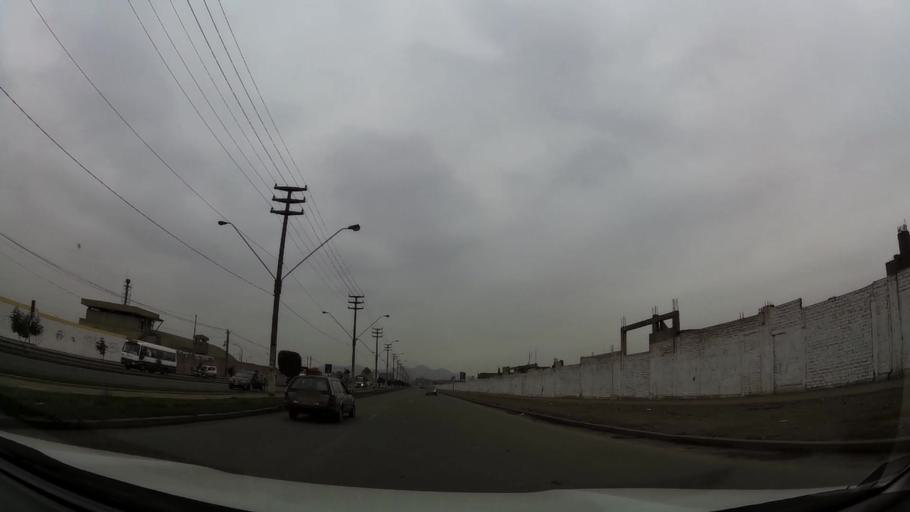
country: PE
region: Lima
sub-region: Lima
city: Vitarte
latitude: -12.0338
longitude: -76.9438
